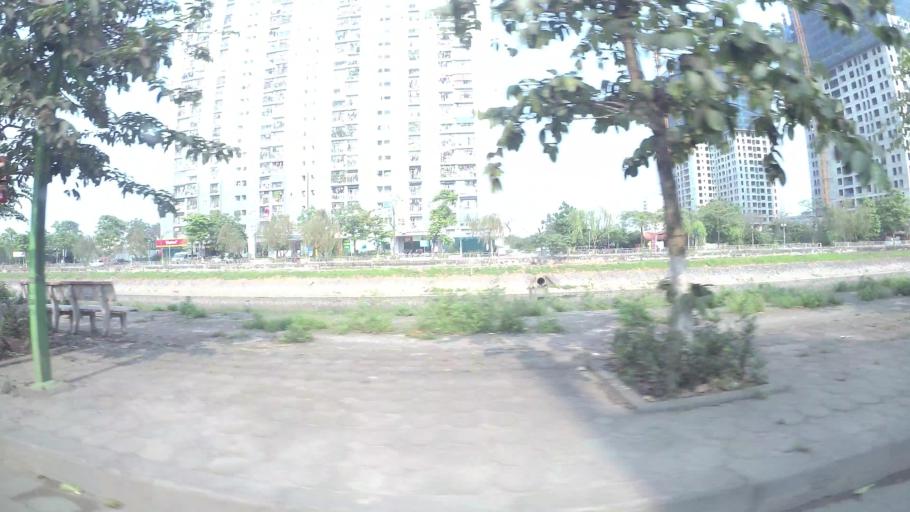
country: VN
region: Ha Noi
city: Thanh Xuan
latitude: 20.9745
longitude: 105.8249
